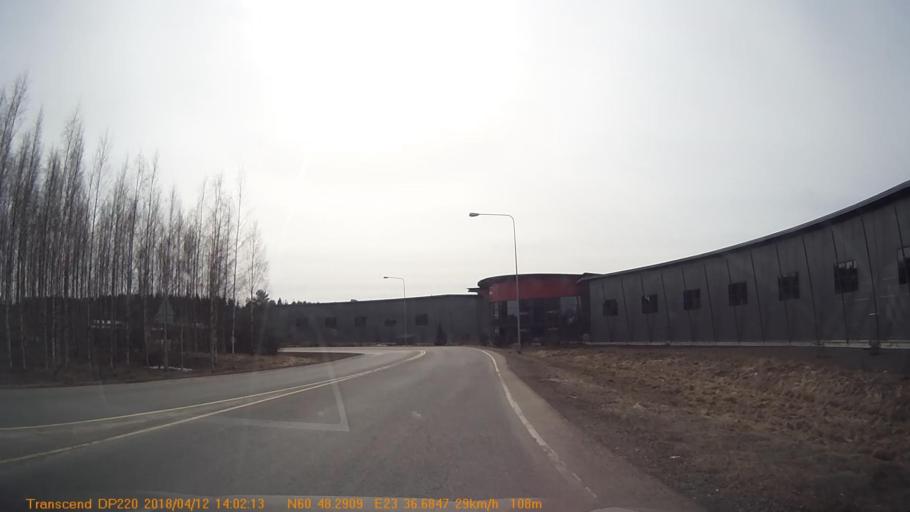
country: FI
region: Haeme
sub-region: Forssa
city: Forssa
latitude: 60.8048
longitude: 23.6112
